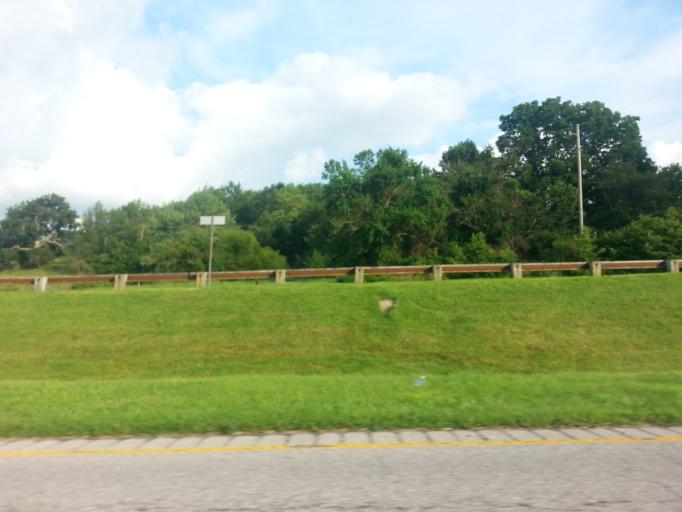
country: US
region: Kentucky
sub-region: Bourbon County
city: Paris
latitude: 38.1561
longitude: -84.3349
